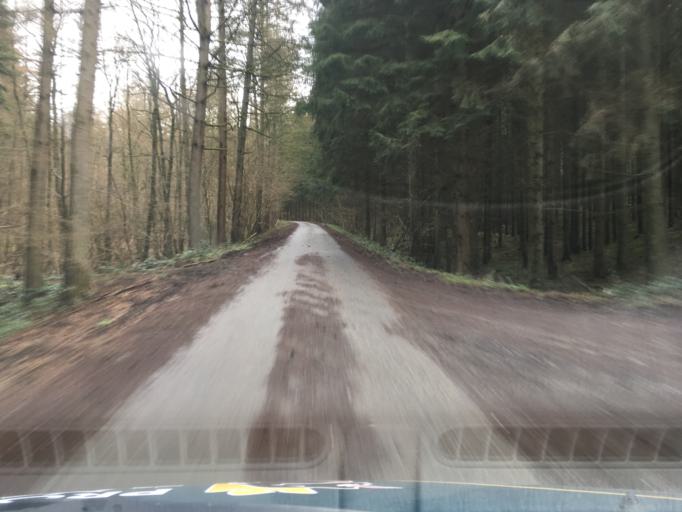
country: FR
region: Champagne-Ardenne
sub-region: Departement des Ardennes
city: Haybes
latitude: 50.0492
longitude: 4.6596
